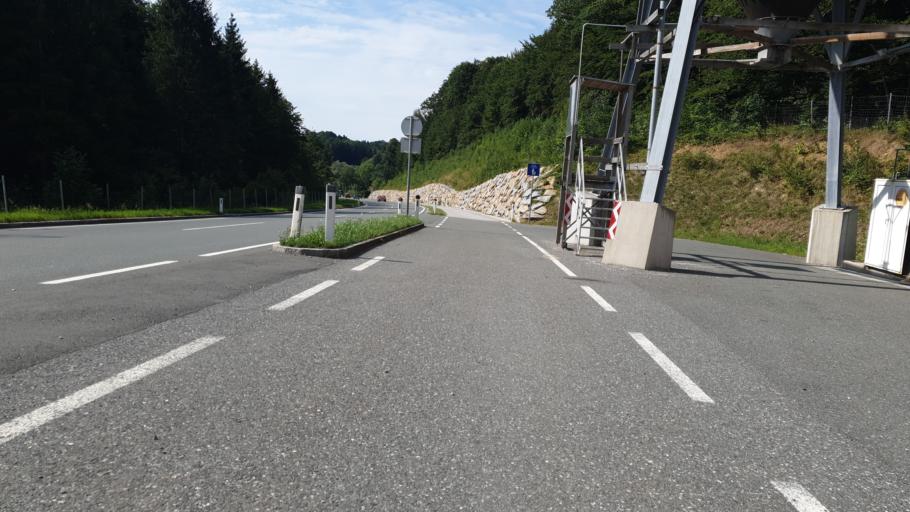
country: AT
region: Salzburg
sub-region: Politischer Bezirk Salzburg-Umgebung
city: Eugendorf
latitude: 47.8751
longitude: 13.1259
